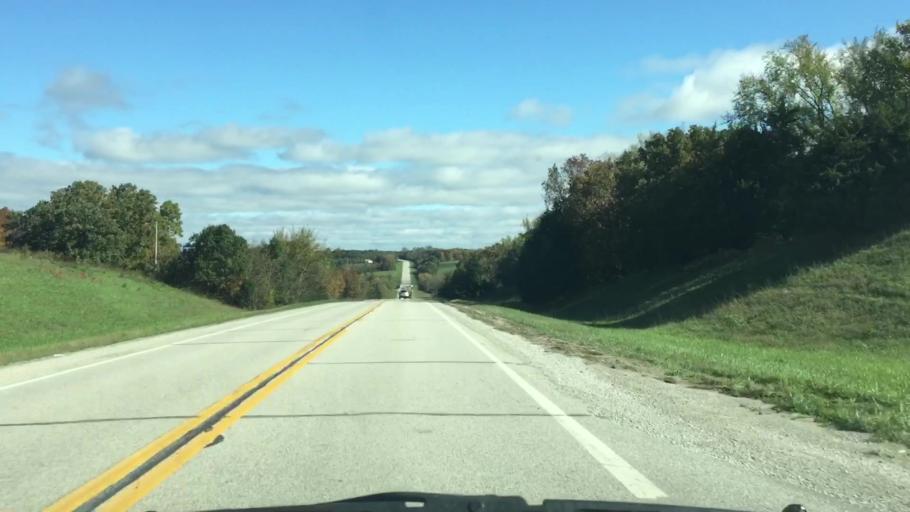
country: US
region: Iowa
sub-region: Decatur County
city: Leon
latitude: 40.6757
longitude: -93.7858
